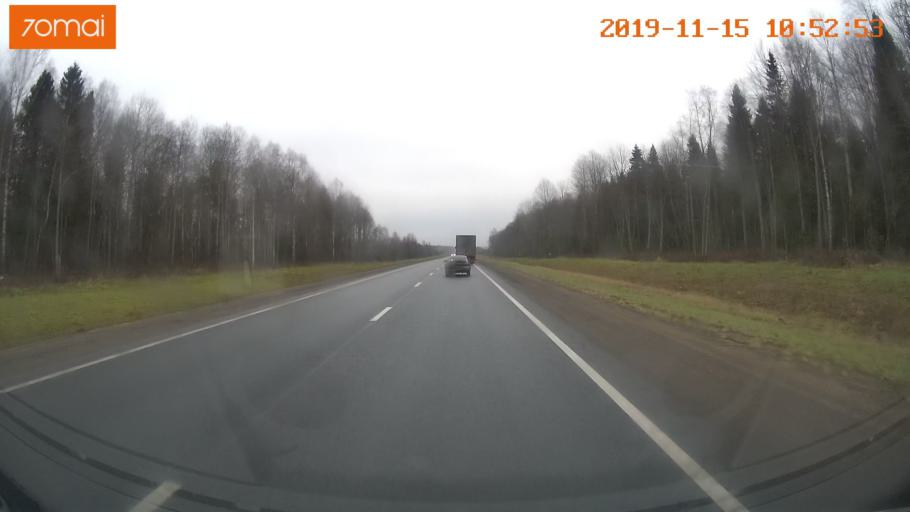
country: RU
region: Vologda
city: Chebsara
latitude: 59.1719
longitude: 38.7423
